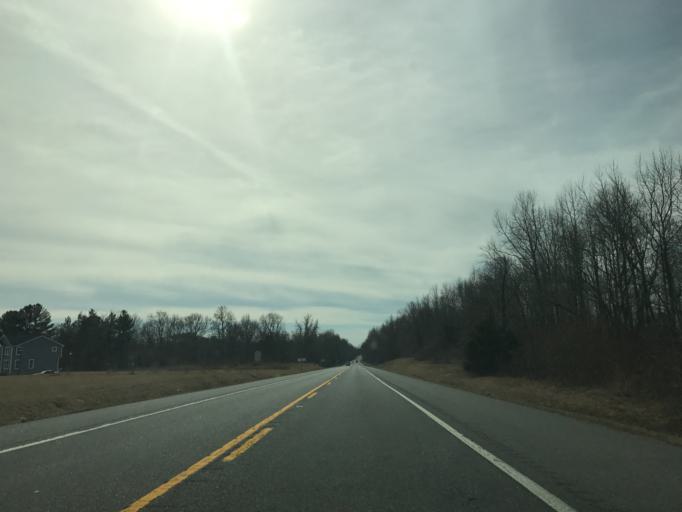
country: US
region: Maryland
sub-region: Queen Anne's County
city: Kingstown
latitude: 39.1478
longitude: -75.9827
